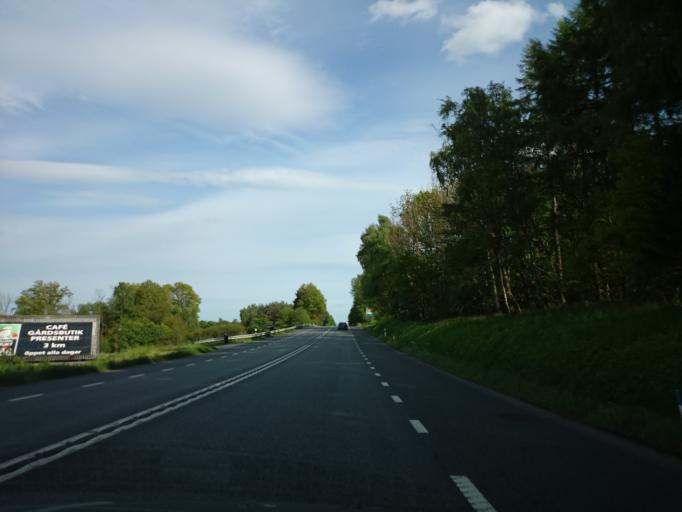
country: SE
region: Skane
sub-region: Kristianstads Kommun
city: Onnestad
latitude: 55.9352
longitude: 13.9168
